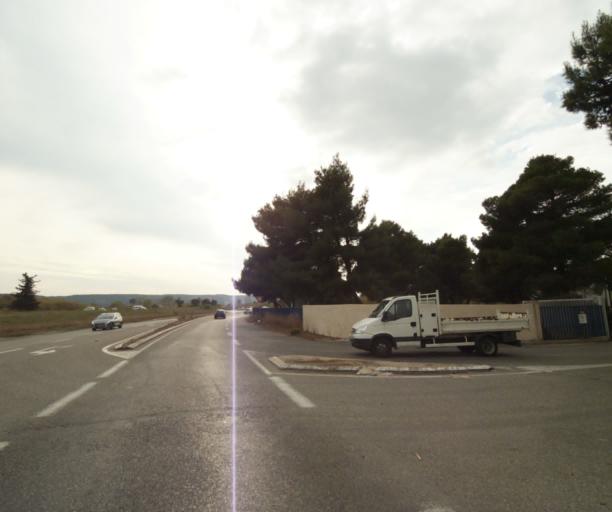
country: FR
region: Provence-Alpes-Cote d'Azur
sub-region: Departement des Bouches-du-Rhone
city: Marignane
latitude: 43.3943
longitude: 5.1952
